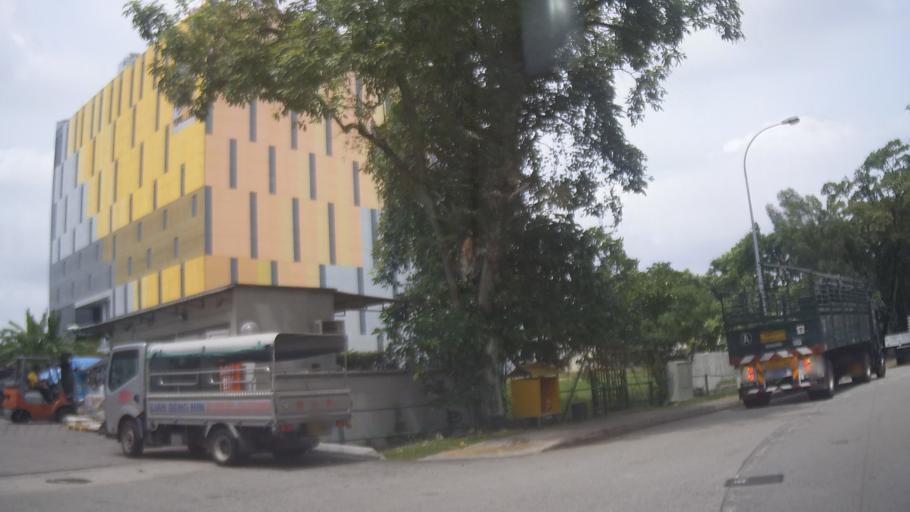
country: MY
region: Johor
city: Johor Bahru
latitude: 1.4123
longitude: 103.7474
